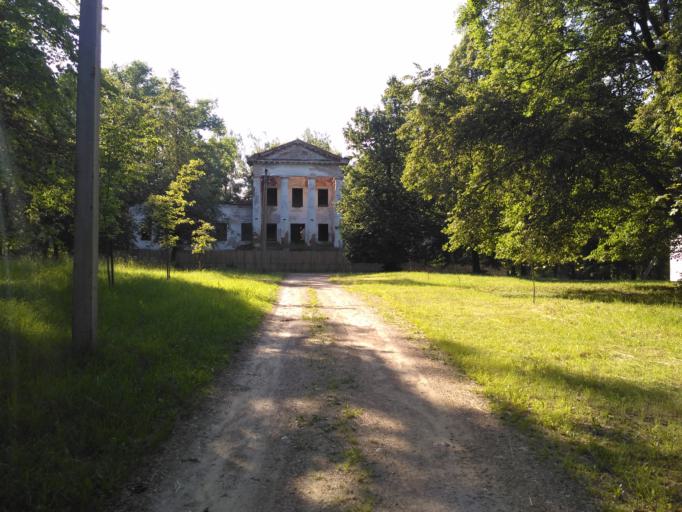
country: BY
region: Minsk
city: Chervyen'
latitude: 53.8840
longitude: 28.6163
